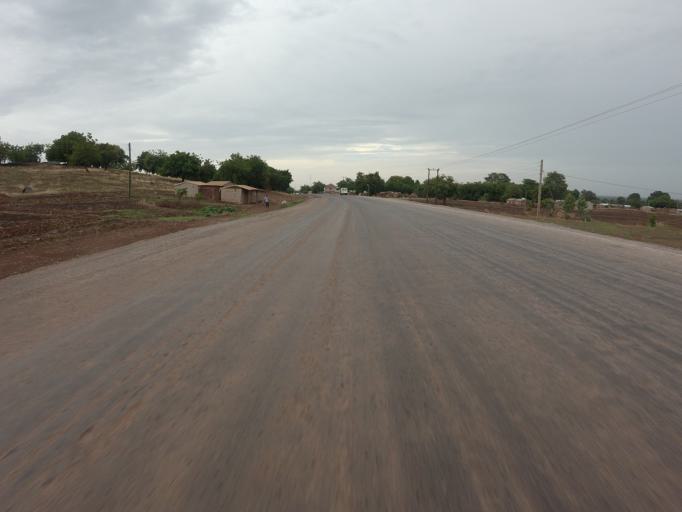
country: GH
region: Upper East
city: Bolgatanga
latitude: 10.8553
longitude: -0.6695
